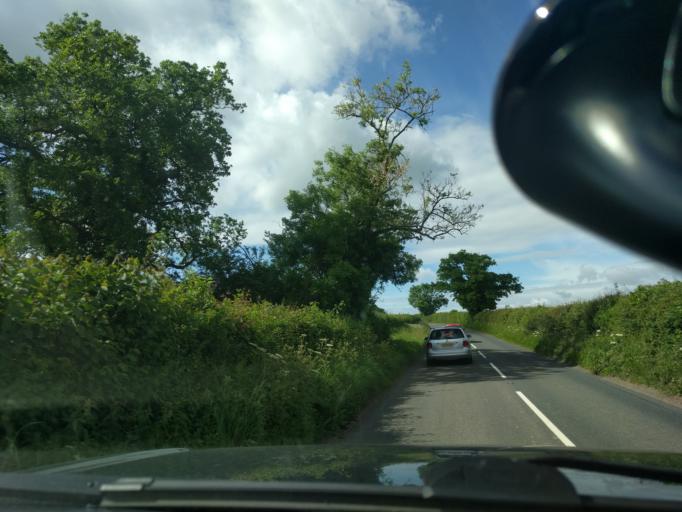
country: GB
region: England
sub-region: Wiltshire
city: Box
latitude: 51.3923
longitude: -2.2329
